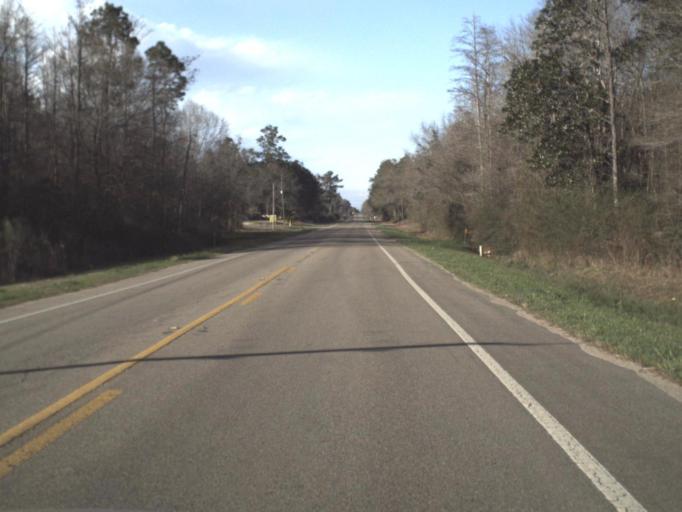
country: US
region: Florida
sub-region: Jackson County
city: Marianna
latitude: 30.7083
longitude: -85.2308
